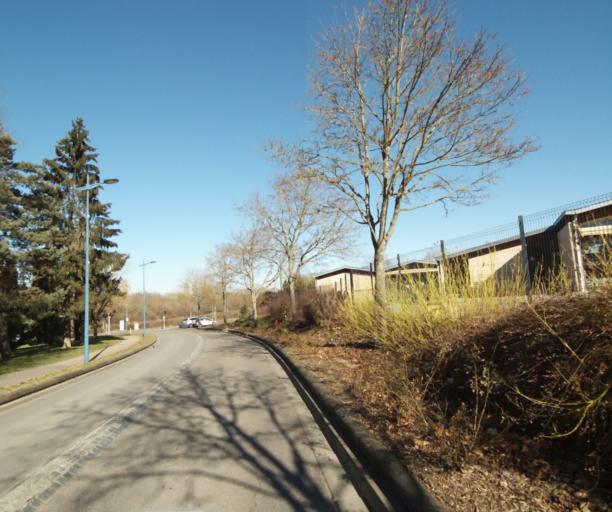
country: FR
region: Lorraine
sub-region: Departement de Meurthe-et-Moselle
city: Vandoeuvre-les-Nancy
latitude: 48.6459
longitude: 6.1973
